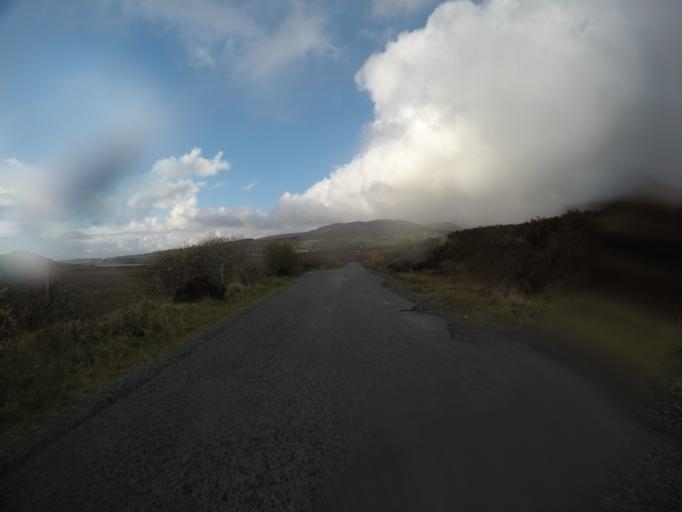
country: GB
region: Scotland
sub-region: Highland
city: Portree
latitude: 57.4703
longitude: -6.2997
